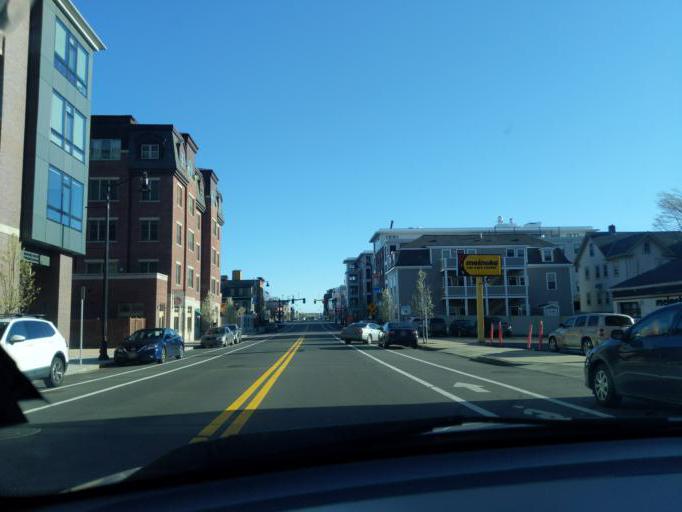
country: US
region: Massachusetts
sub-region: Essex County
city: Beverly
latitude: 42.5454
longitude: -70.8847
